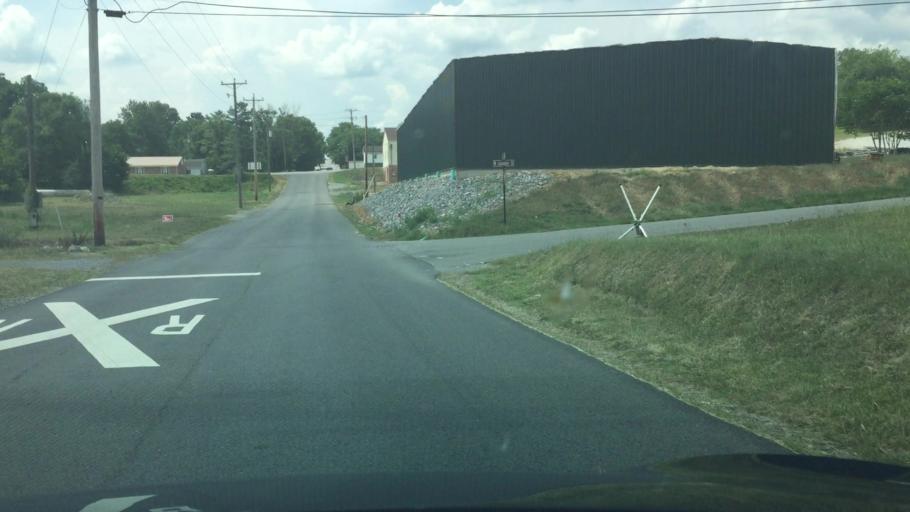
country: US
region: Virginia
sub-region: Wythe County
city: Wytheville
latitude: 36.9421
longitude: -81.0793
